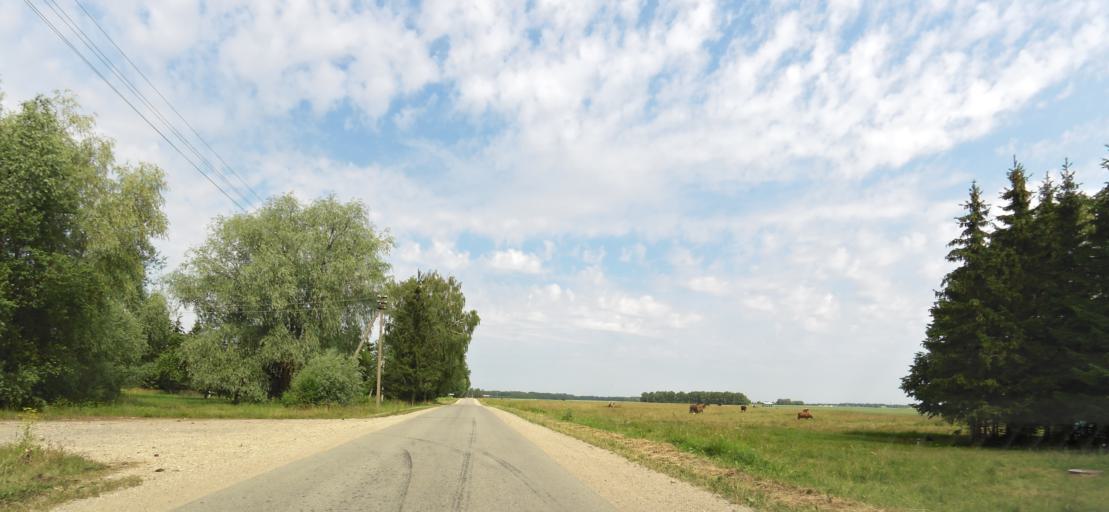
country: LT
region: Panevezys
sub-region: Birzai
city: Birzai
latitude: 56.2665
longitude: 24.6067
